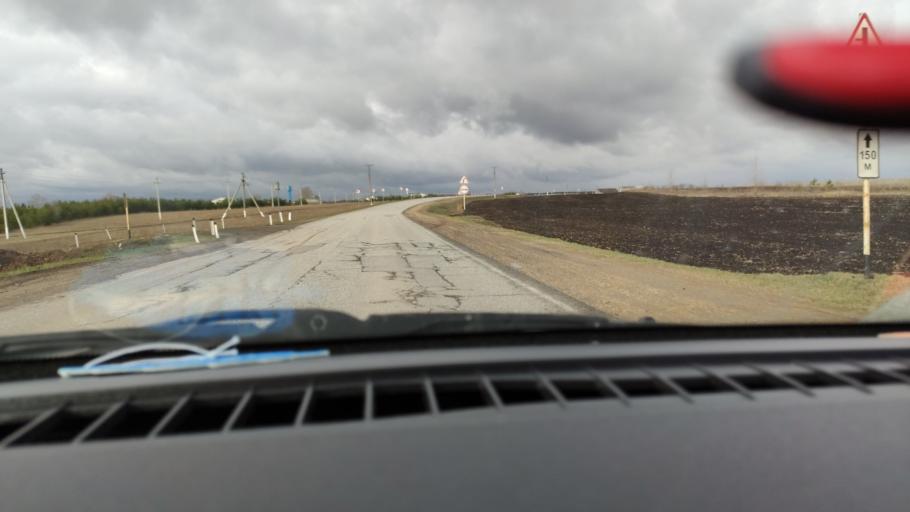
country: RU
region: Tatarstan
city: Cheremshan
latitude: 54.8304
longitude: 51.5557
